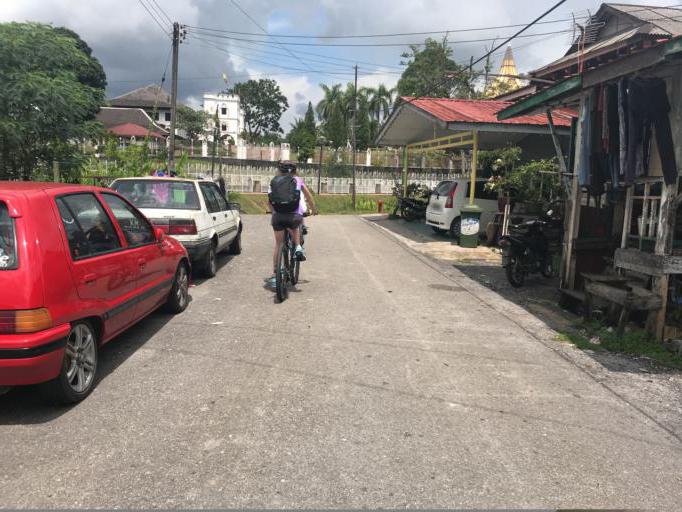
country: MY
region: Sarawak
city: Kuching
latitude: 1.5633
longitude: 110.3441
